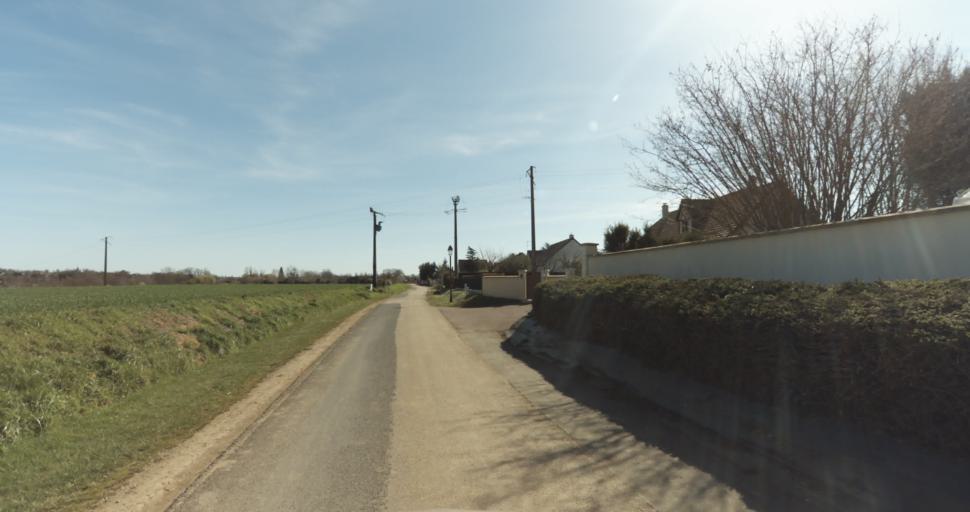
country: FR
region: Lower Normandy
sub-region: Departement du Calvados
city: Saint-Pierre-sur-Dives
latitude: 49.0450
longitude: -0.0265
